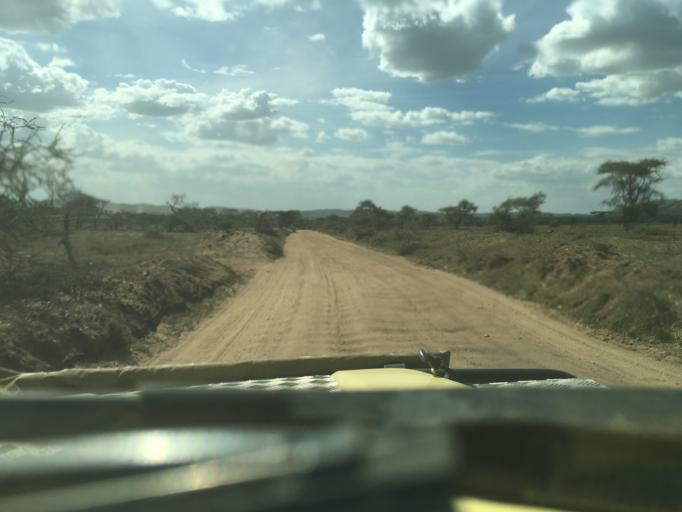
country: TZ
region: Mara
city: Mugumu
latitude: -2.4288
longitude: 34.8246
